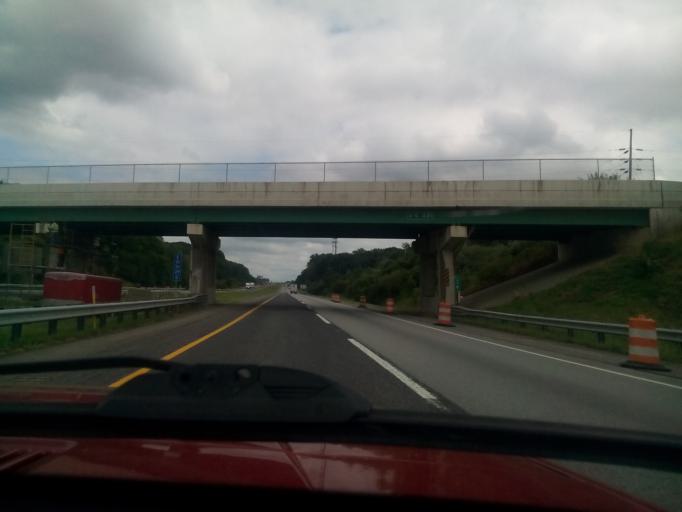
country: US
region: Indiana
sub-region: LaPorte County
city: Westville
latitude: 41.5904
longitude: -86.8977
